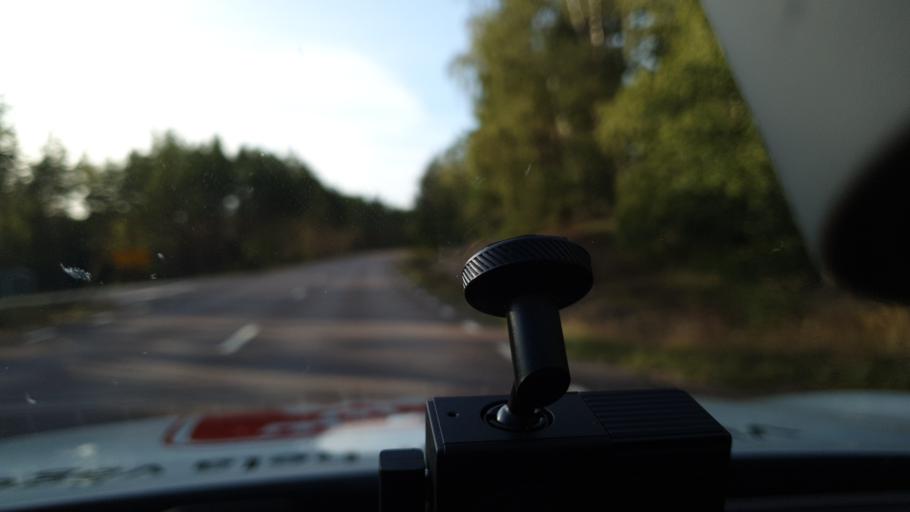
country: SE
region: Kalmar
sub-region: Kalmar Kommun
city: Trekanten
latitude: 56.8792
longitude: 16.1052
